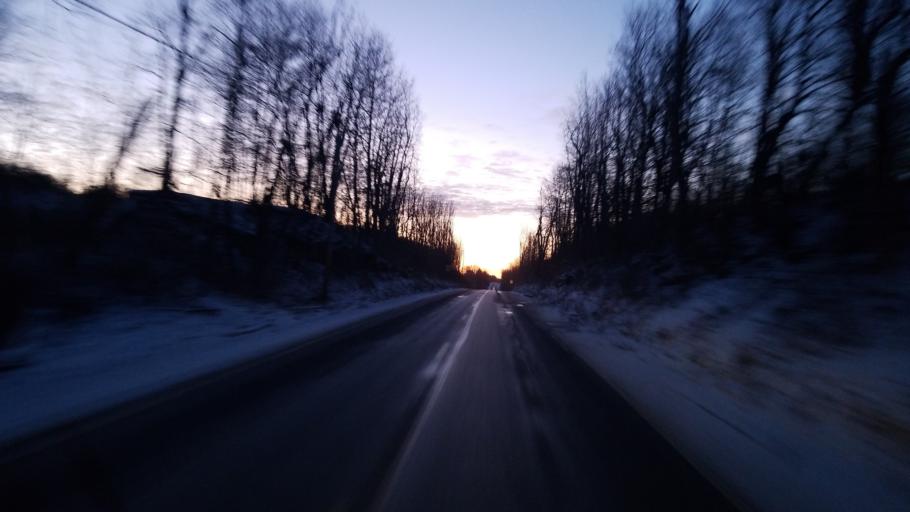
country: US
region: Pennsylvania
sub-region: Clarion County
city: Knox
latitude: 41.2682
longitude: -79.5654
